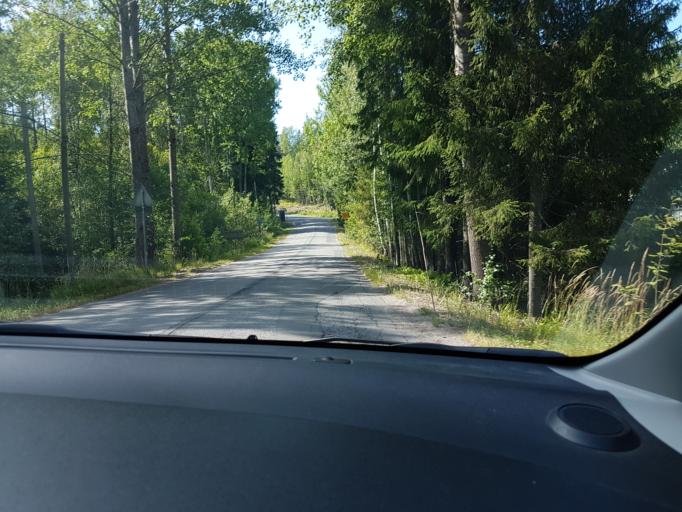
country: FI
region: Uusimaa
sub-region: Helsinki
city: Kilo
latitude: 60.3310
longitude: 24.7727
